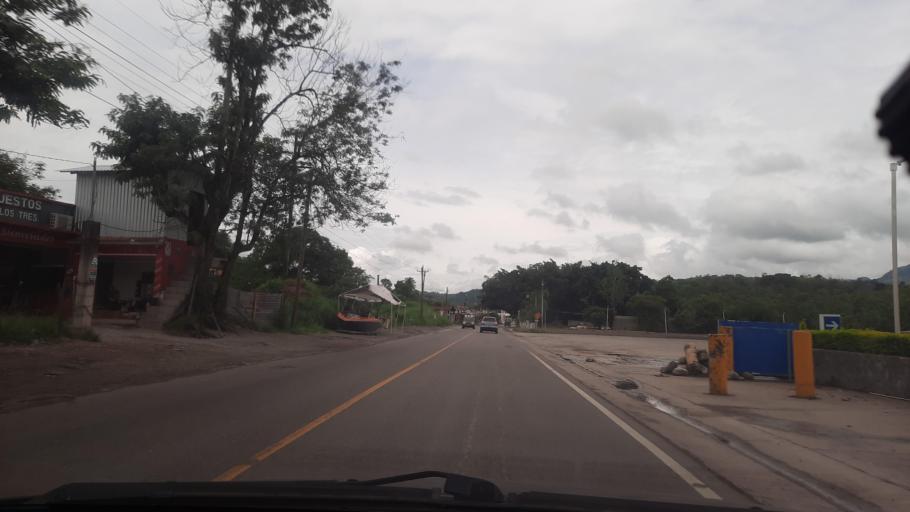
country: GT
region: Izabal
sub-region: Municipio de Los Amates
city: Los Amates
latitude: 15.2538
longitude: -89.1022
